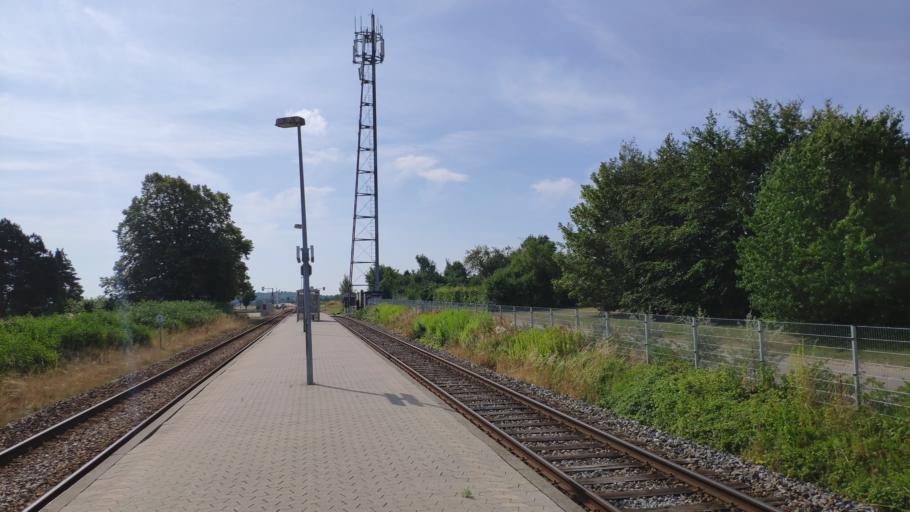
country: DK
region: Capital Region
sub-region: Halsnaes Kommune
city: Frederiksvaerk
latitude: 55.9355
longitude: 12.0459
